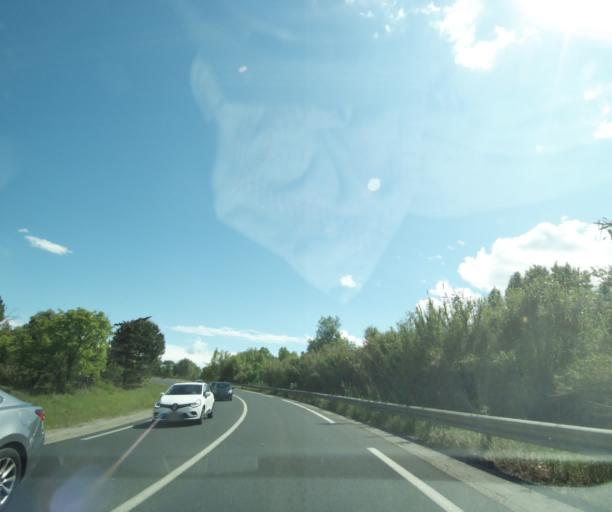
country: FR
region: Languedoc-Roussillon
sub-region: Departement de l'Herault
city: Saint-Jean-de-Vedas
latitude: 43.5909
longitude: 3.8208
